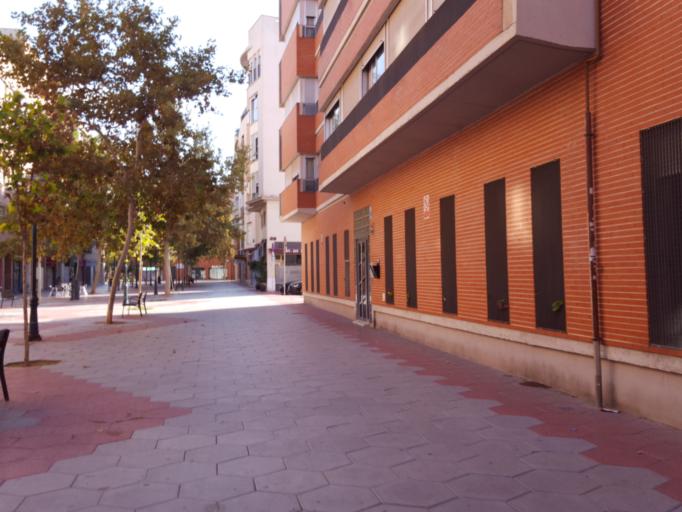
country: ES
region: Murcia
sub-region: Murcia
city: Murcia
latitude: 37.9954
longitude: -1.1198
